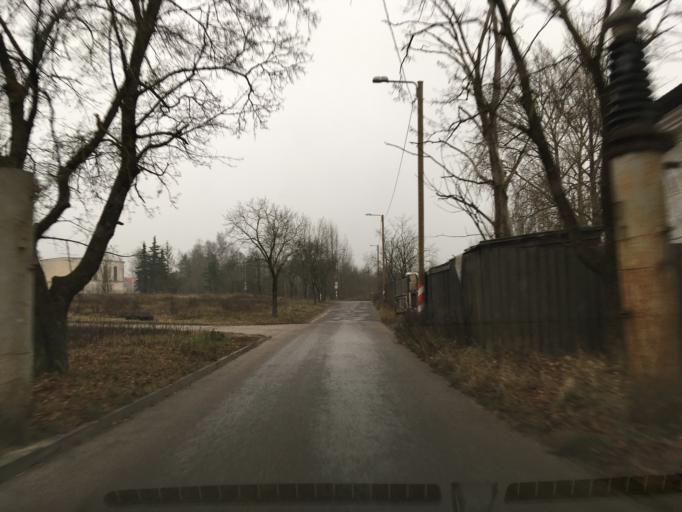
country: EE
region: Harju
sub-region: Tallinna linn
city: Tallinn
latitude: 59.3989
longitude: 24.7186
